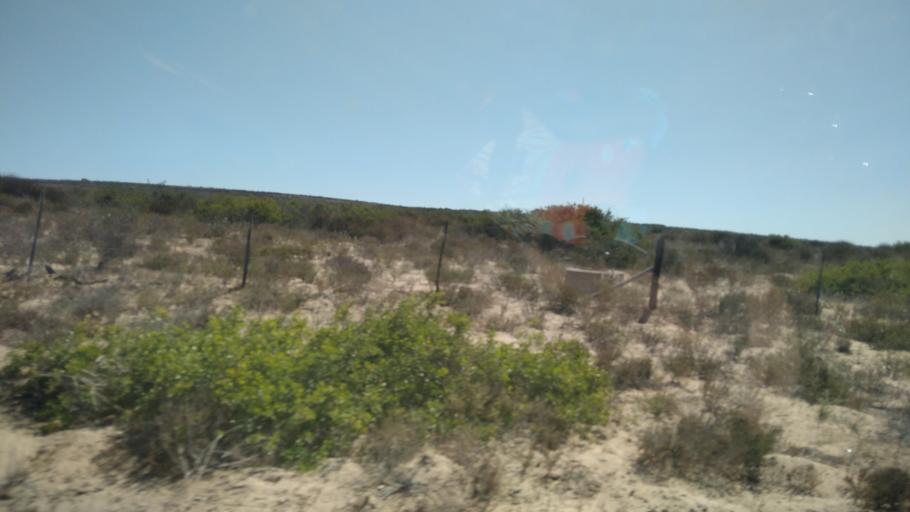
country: ZA
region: Western Cape
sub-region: West Coast District Municipality
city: Vredenburg
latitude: -33.0065
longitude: 18.1215
